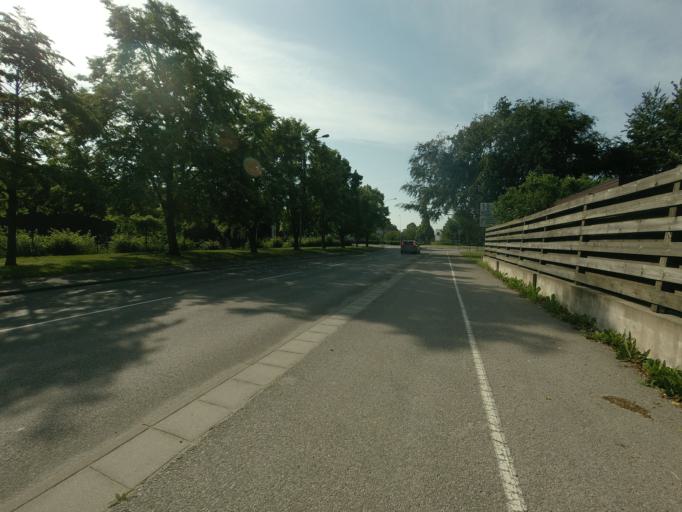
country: SE
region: Skane
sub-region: Vellinge Kommun
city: Vellinge
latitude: 55.4759
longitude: 13.0163
